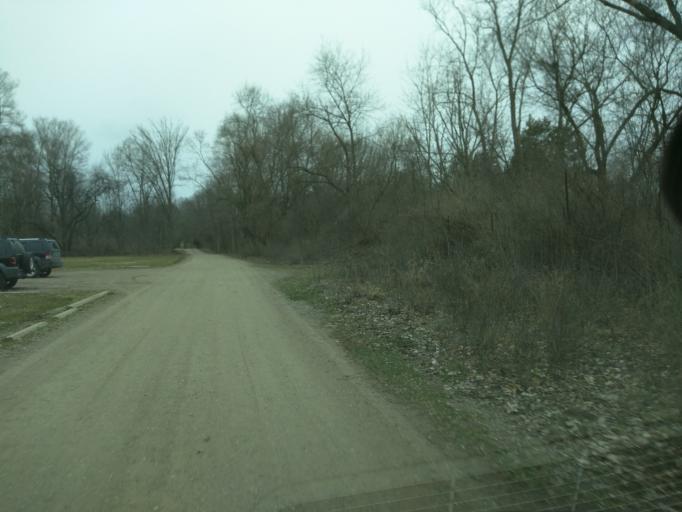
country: US
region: Michigan
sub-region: Eaton County
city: Waverly
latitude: 42.7597
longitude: -84.6125
